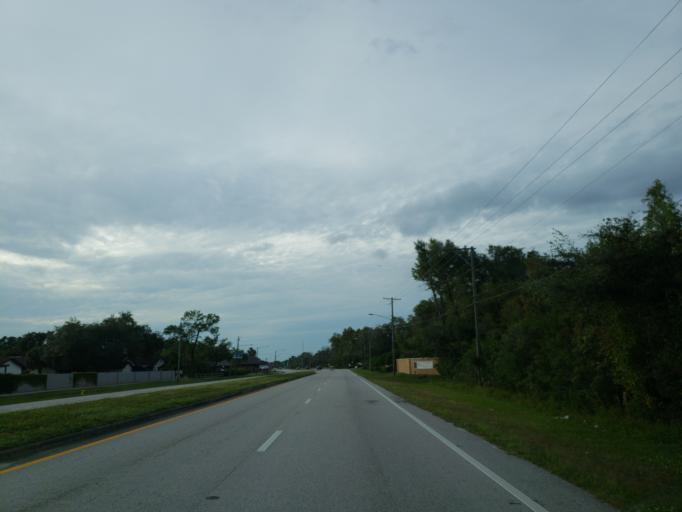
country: US
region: Florida
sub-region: Hillsborough County
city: Carrollwood Village
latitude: 28.0544
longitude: -82.5268
